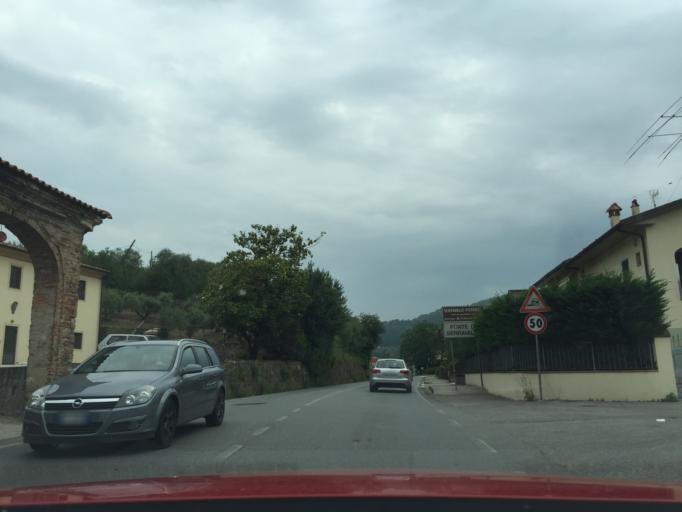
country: IT
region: Tuscany
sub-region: Provincia di Pistoia
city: Pieve a Nievole
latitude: 43.8898
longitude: 10.8154
